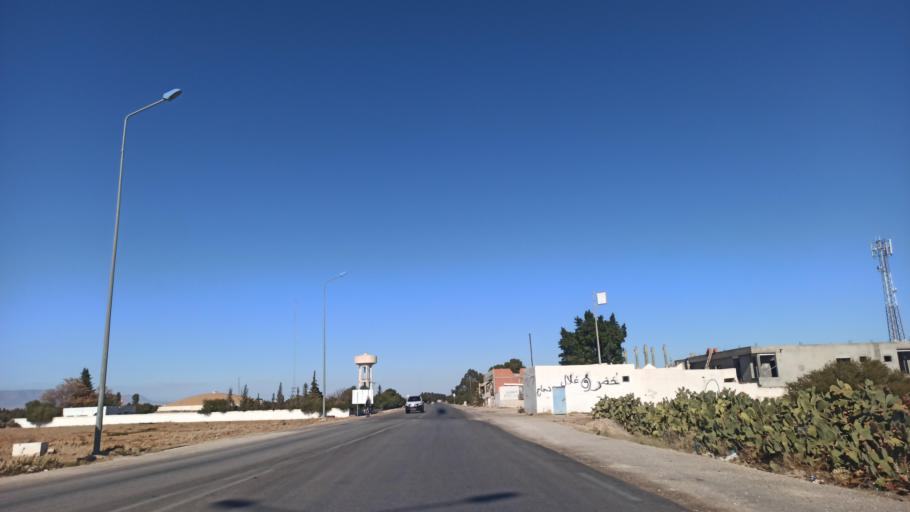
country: TN
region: Sidi Bu Zayd
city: Jilma
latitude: 35.1477
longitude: 9.3634
